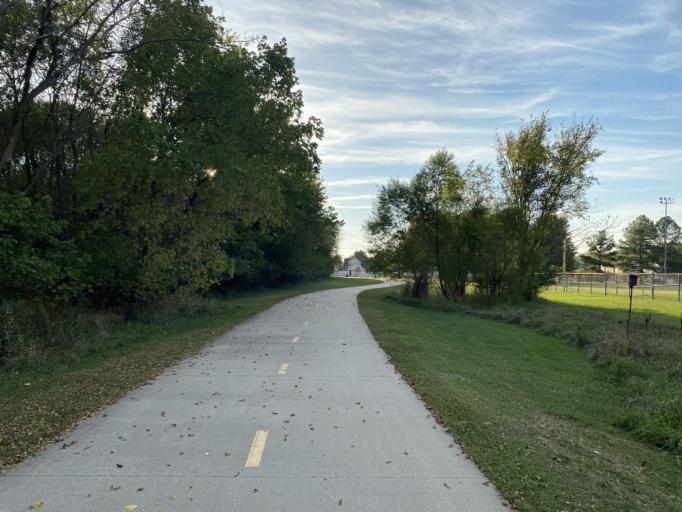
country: US
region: Arkansas
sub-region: Washington County
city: Johnson
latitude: 36.1022
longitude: -94.2060
